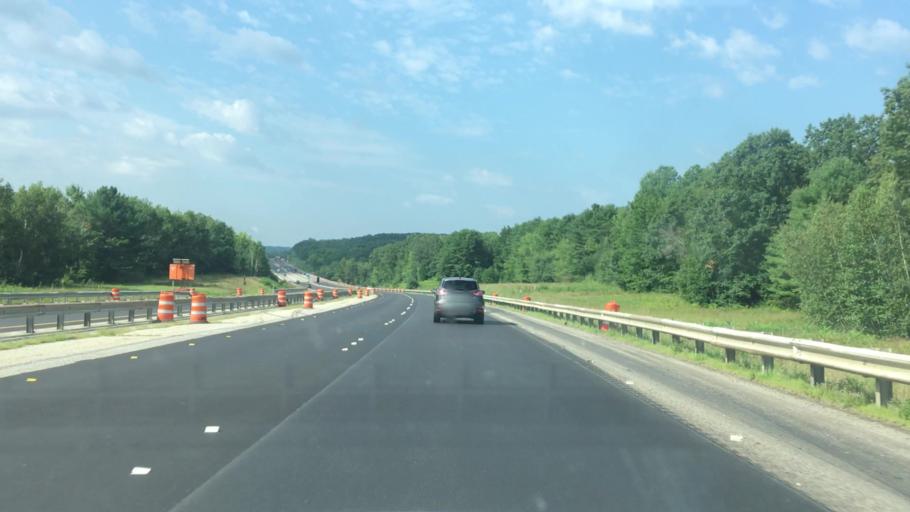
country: US
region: Maine
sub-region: Androscoggin County
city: Lewiston
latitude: 44.0690
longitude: -70.2017
